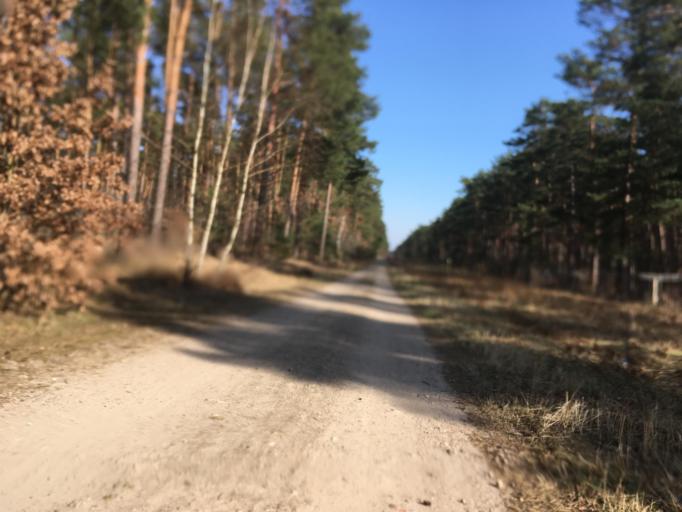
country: DE
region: Brandenburg
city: Wandlitz
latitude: 52.6923
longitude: 13.4526
